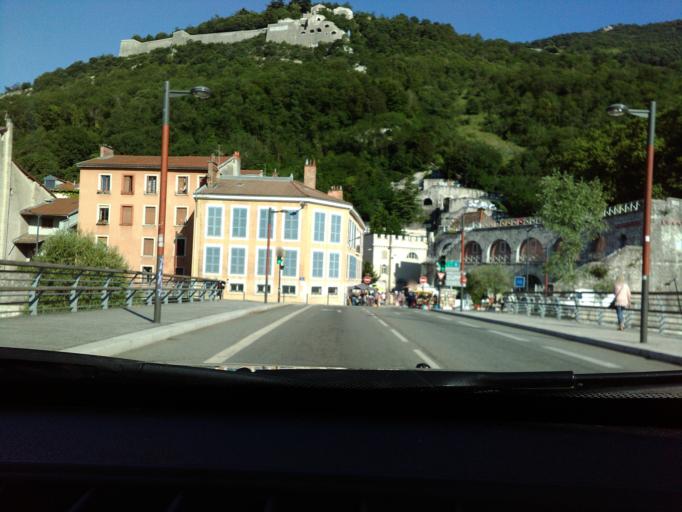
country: FR
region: Rhone-Alpes
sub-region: Departement de l'Isere
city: La Tronche
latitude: 45.1974
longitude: 5.7330
